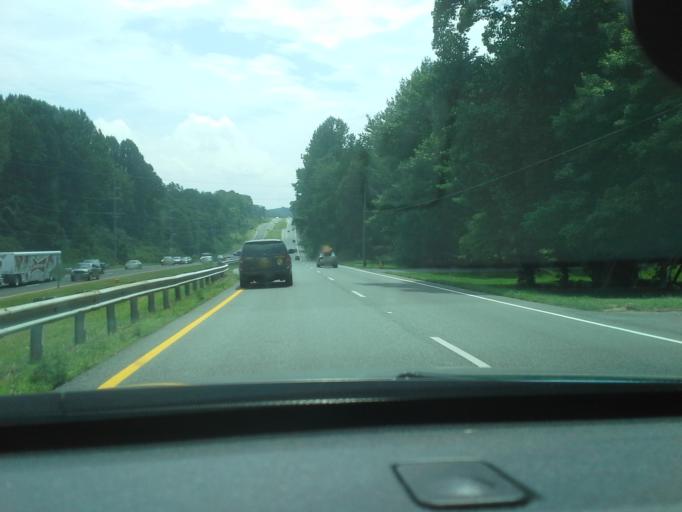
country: US
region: Maryland
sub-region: Calvert County
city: Dunkirk Town Center
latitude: 38.7019
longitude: -76.6465
